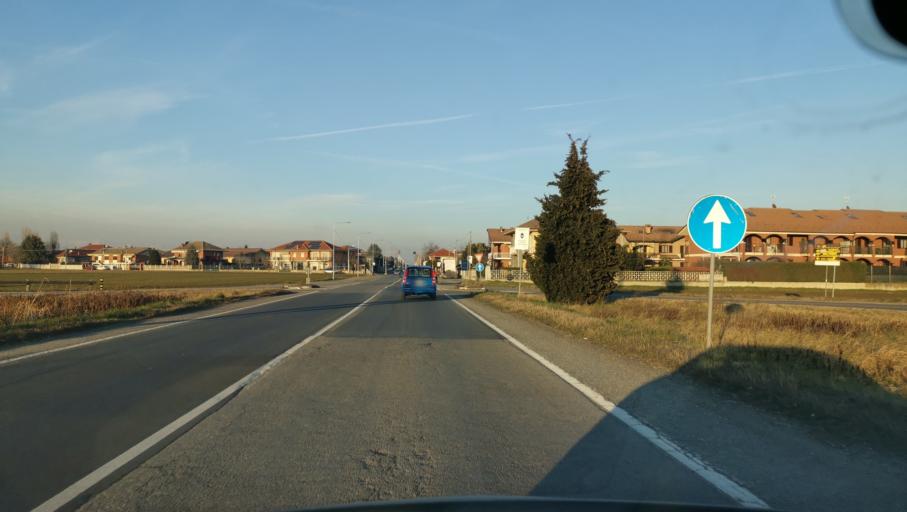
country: IT
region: Piedmont
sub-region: Provincia di Torino
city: Gerbole-Zucche
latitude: 44.9767
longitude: 7.5238
